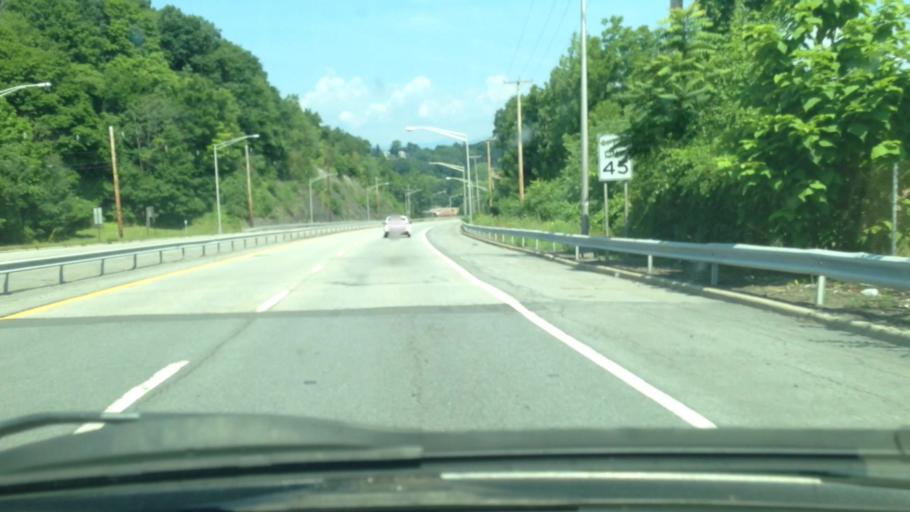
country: US
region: New York
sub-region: Ulster County
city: Port Ewen
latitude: 41.9141
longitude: -73.9788
